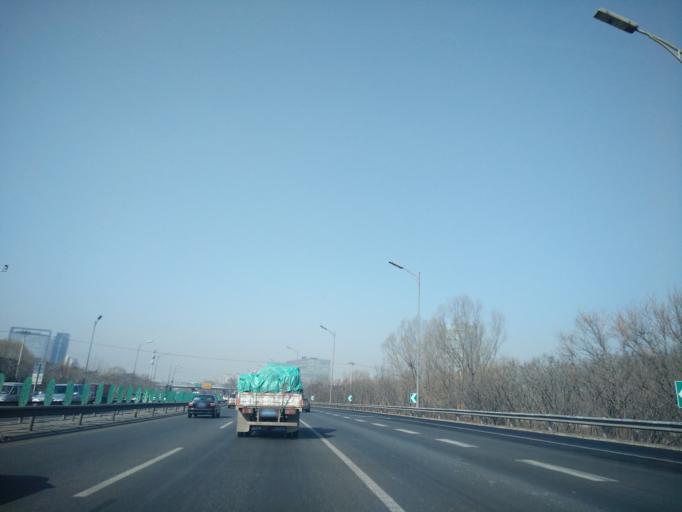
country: CN
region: Beijing
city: Wangjing
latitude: 40.0133
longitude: 116.4760
